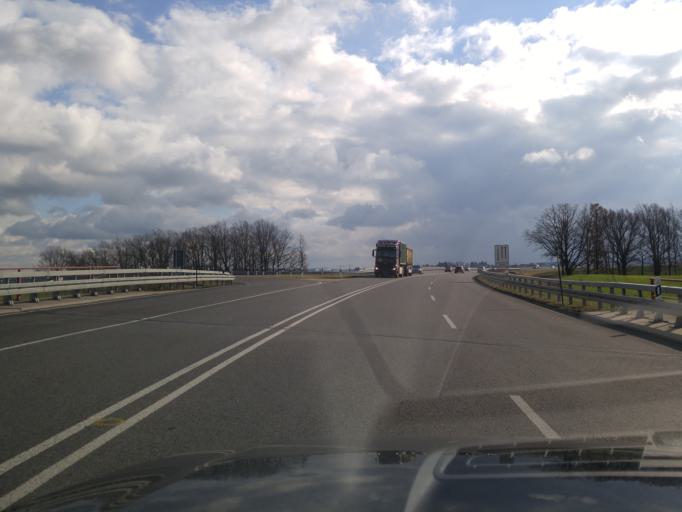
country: DE
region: Saxony
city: Lichtentanne
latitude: 50.6831
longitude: 12.4459
